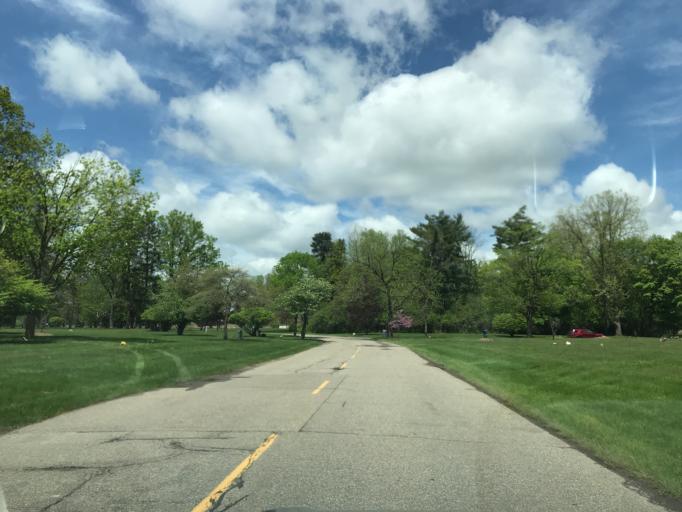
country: US
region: Michigan
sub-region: Oakland County
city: Franklin
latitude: 42.4834
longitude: -83.2999
